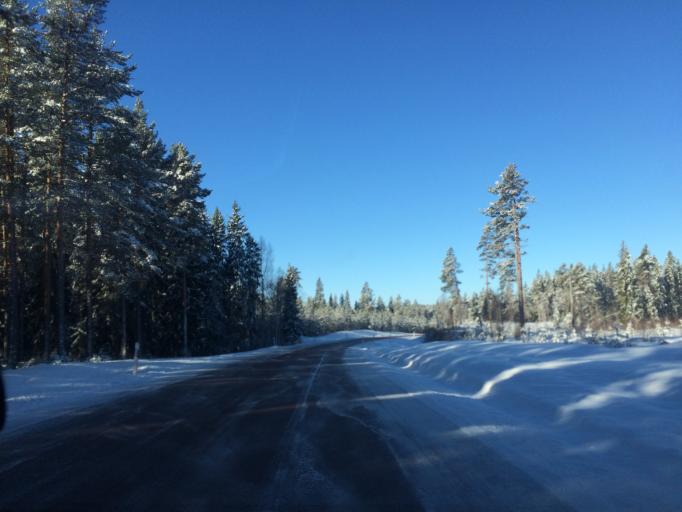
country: SE
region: Dalarna
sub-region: Mora Kommun
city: Mora
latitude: 60.8473
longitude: 14.2754
